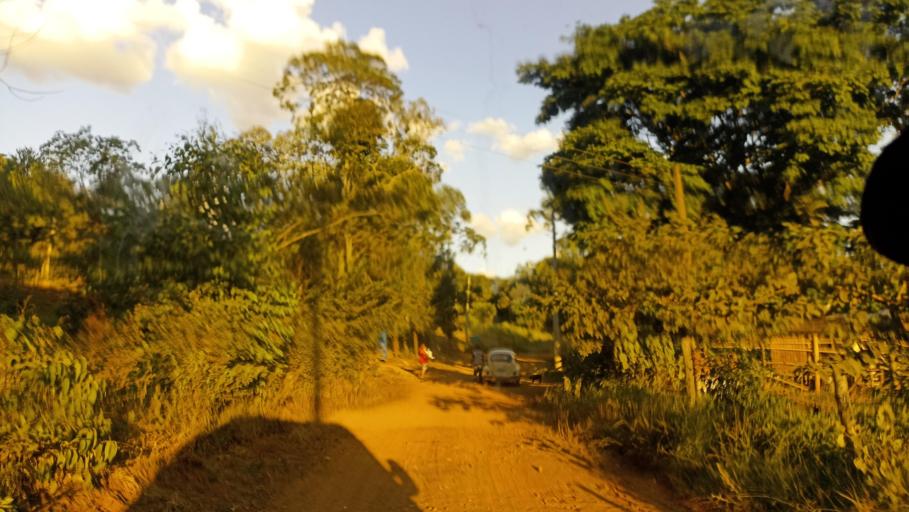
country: BR
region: Minas Gerais
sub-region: Sao Joao Del Rei
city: Sao Joao del Rei
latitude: -21.1835
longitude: -44.3499
